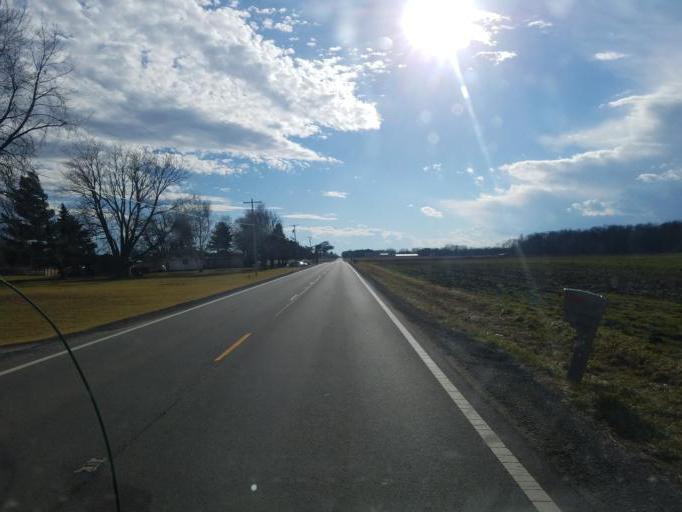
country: US
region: Ohio
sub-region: Marion County
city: Marion
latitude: 40.5369
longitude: -83.0538
